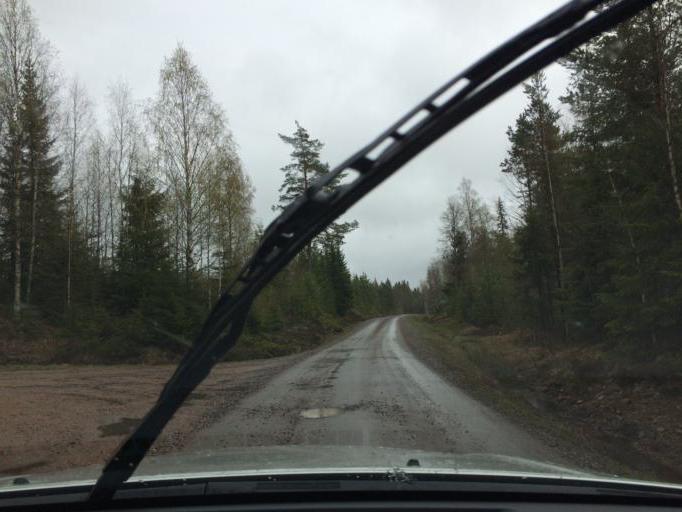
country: SE
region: OErebro
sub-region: Hallefors Kommun
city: Haellefors
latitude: 60.0329
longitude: 14.5459
